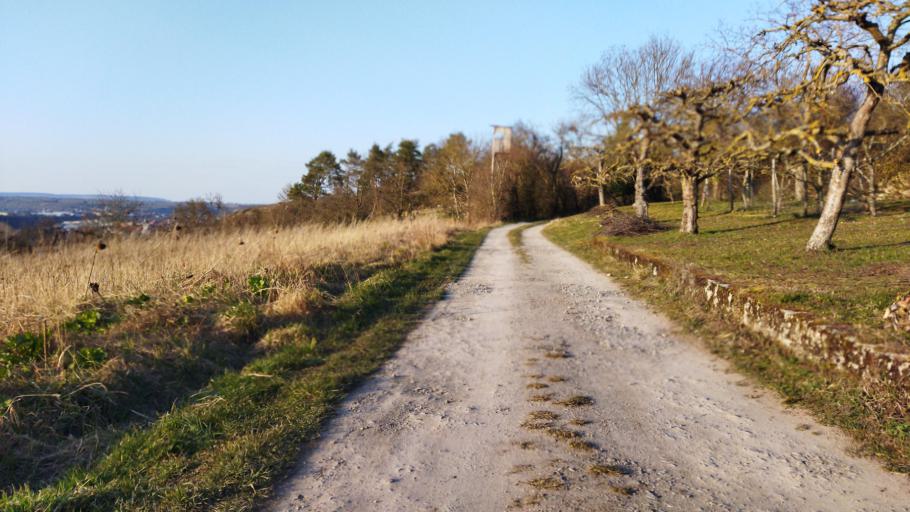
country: DE
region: Baden-Wuerttemberg
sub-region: Regierungsbezirk Stuttgart
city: Walheim
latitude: 49.0121
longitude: 9.1629
